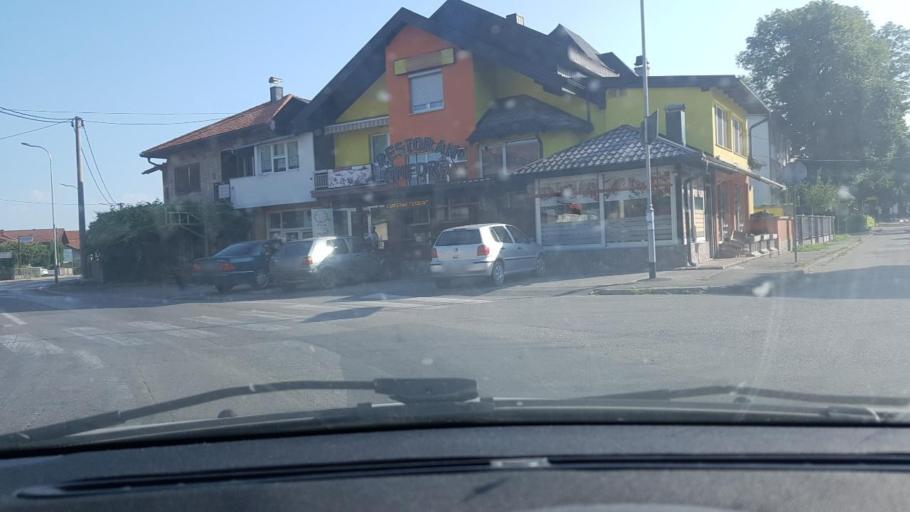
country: BA
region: Federation of Bosnia and Herzegovina
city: Bihac
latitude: 44.8168
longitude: 15.8818
